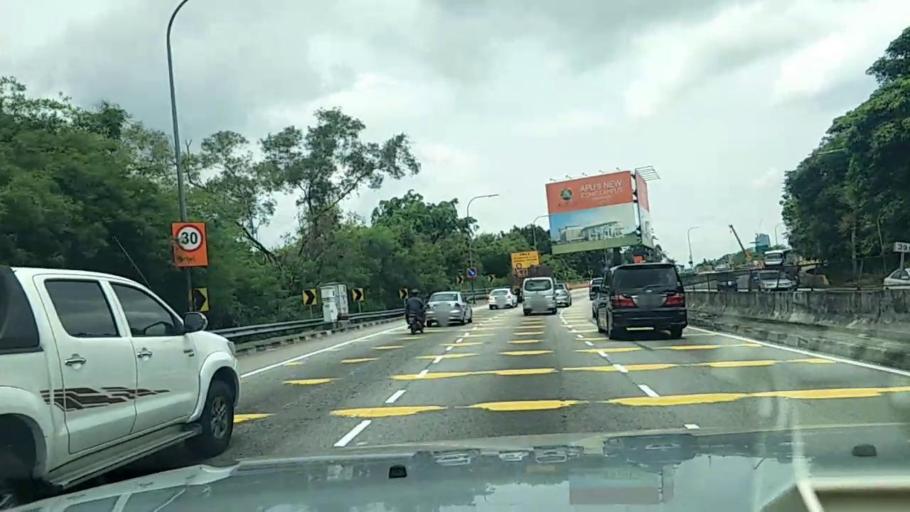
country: MY
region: Selangor
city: Kampong Baharu Balakong
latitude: 3.0685
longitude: 101.7093
